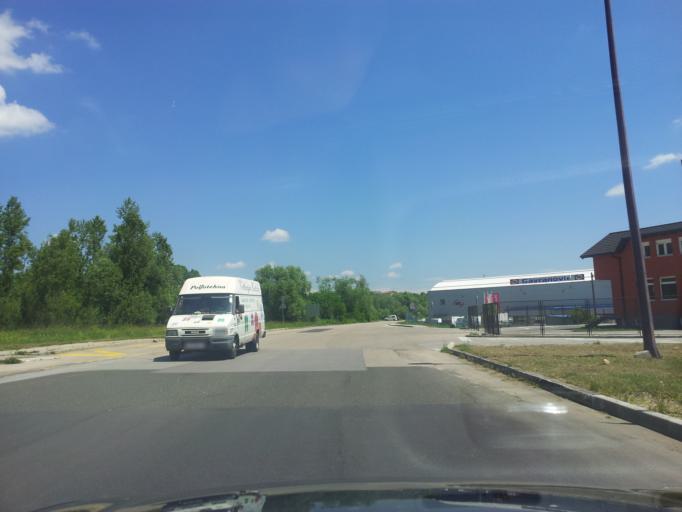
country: HR
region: Karlovacka
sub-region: Grad Karlovac
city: Karlovac
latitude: 45.4628
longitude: 15.5330
